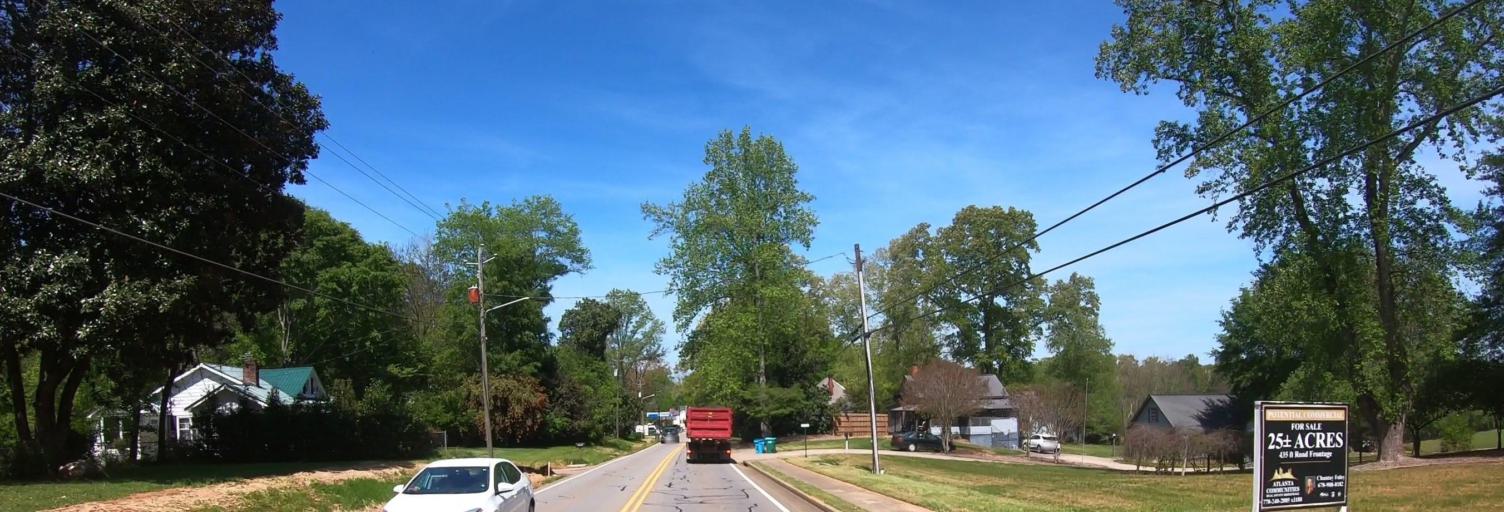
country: US
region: Georgia
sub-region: Cherokee County
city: Canton
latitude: 34.3134
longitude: -84.5473
